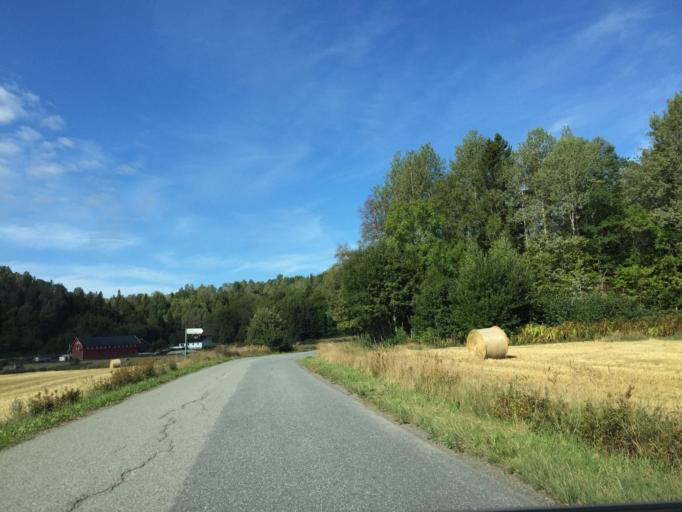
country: NO
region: Vestfold
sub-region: Hof
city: Hof
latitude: 59.4843
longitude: 10.1619
